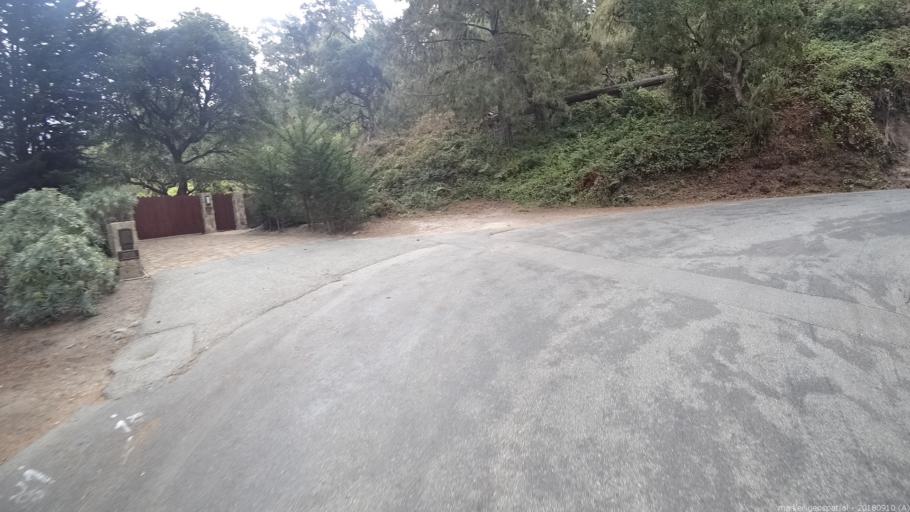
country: US
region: California
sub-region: Monterey County
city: Carmel-by-the-Sea
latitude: 36.4969
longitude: -121.9353
